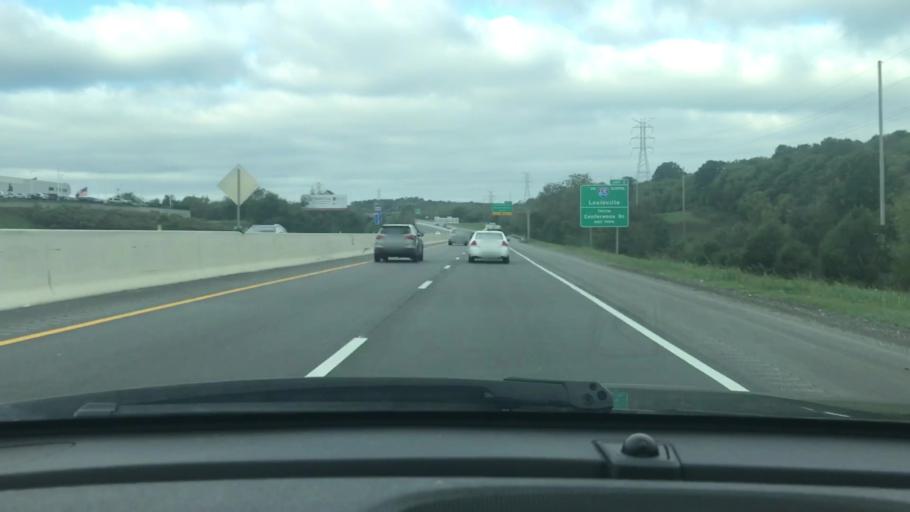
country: US
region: Tennessee
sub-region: Davidson County
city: Goodlettsville
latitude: 36.3123
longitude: -86.6752
